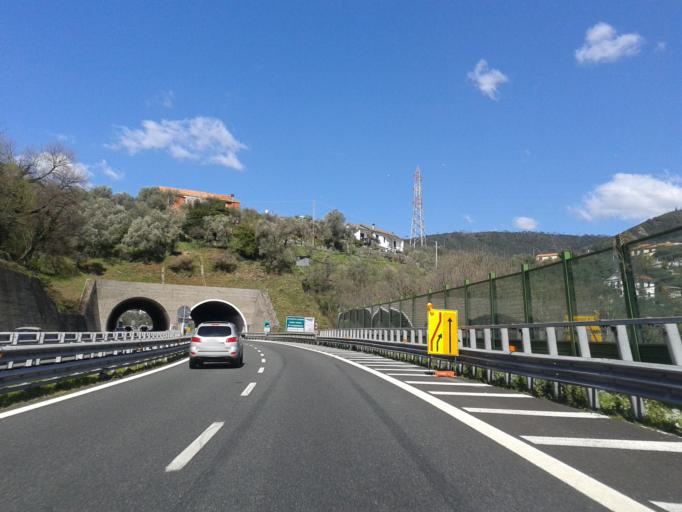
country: IT
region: Liguria
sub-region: Provincia di Genova
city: Sestri Levante
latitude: 44.2789
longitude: 9.4162
